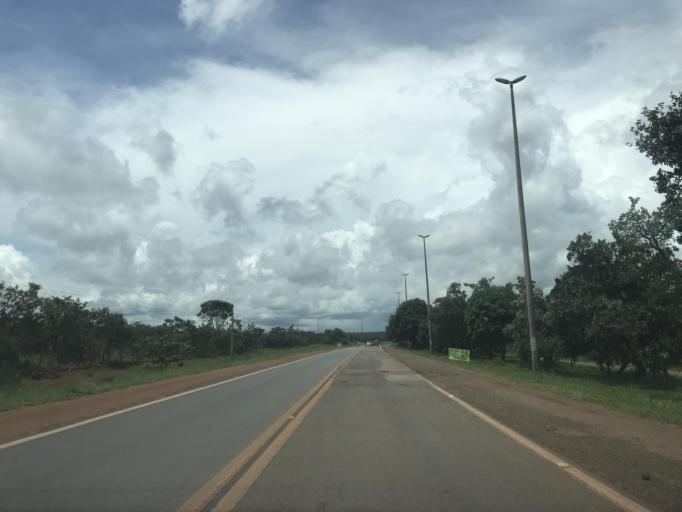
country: BR
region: Federal District
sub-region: Brasilia
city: Brasilia
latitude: -15.6909
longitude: -47.8311
